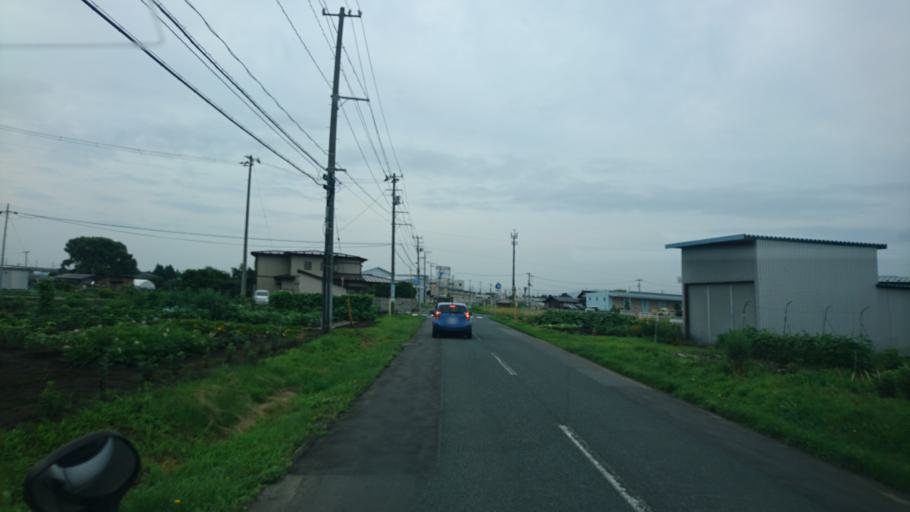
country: JP
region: Iwate
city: Morioka-shi
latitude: 39.6611
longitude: 141.1416
